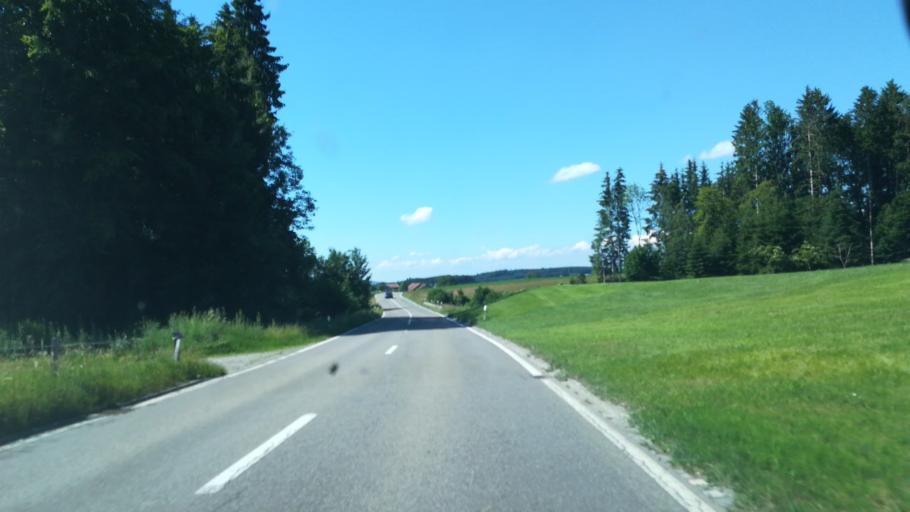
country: CH
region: Saint Gallen
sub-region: Wahlkreis St. Gallen
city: Andwil
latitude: 47.4532
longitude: 9.2534
